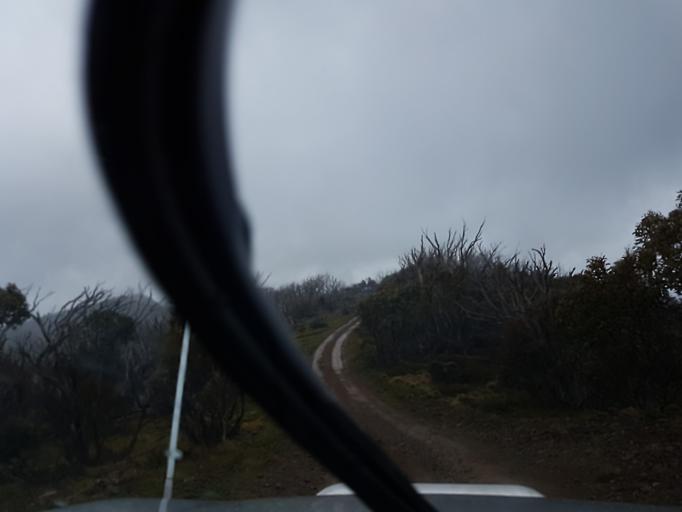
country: AU
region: Victoria
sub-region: Alpine
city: Mount Beauty
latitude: -37.0940
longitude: 147.0610
